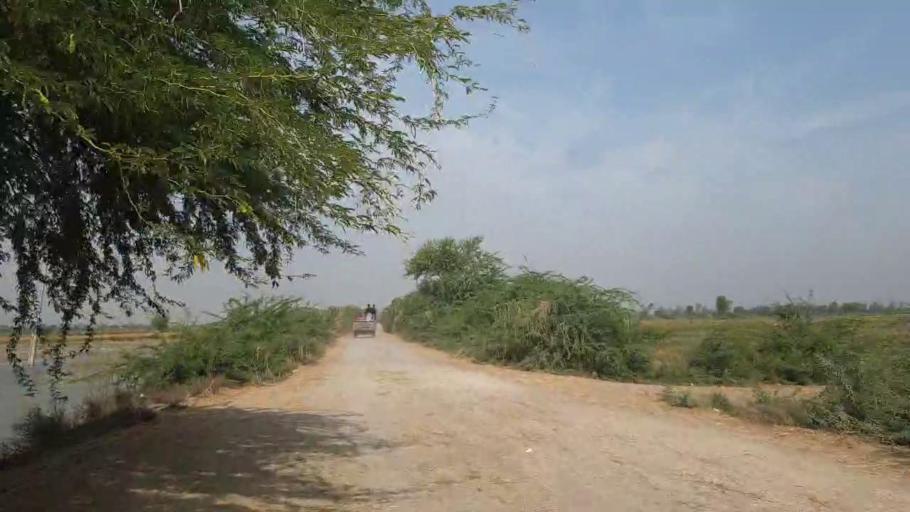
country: PK
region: Sindh
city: Tando Bago
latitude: 24.9138
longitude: 68.9959
